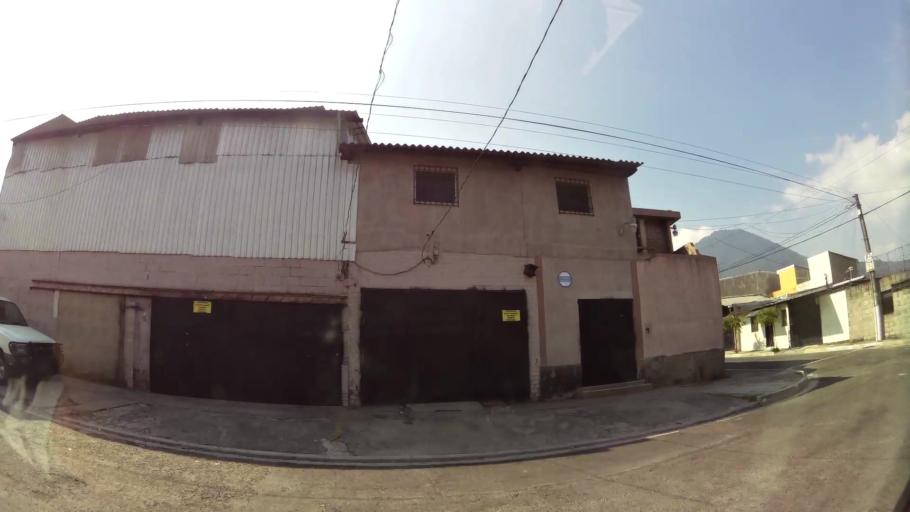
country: SV
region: San Salvador
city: Mejicanos
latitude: 13.7199
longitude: -89.2171
